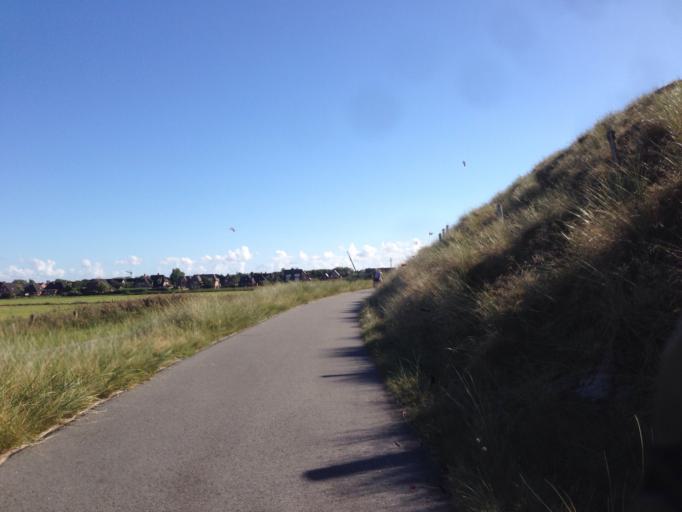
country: DE
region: Schleswig-Holstein
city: List
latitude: 55.0274
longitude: 8.4187
